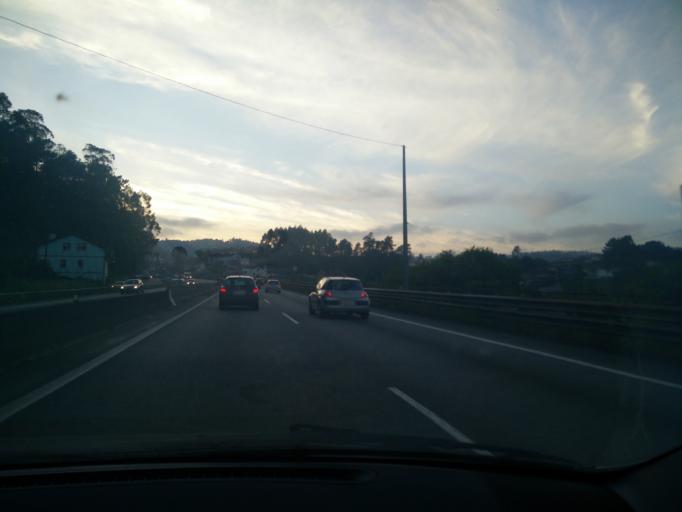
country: ES
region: Galicia
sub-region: Provincia de Pontevedra
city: Porrino
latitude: 42.1931
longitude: -8.6420
